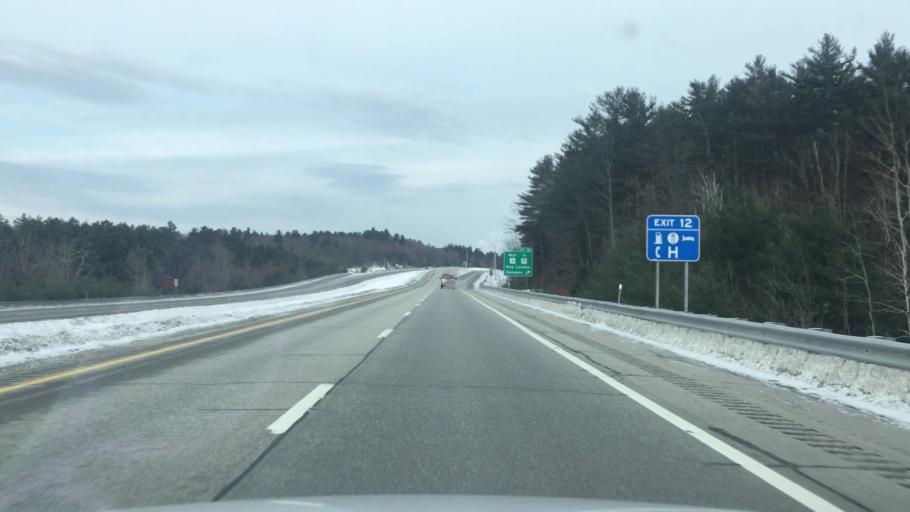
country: US
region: New Hampshire
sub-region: Merrimack County
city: New London
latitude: 43.4175
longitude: -72.0330
